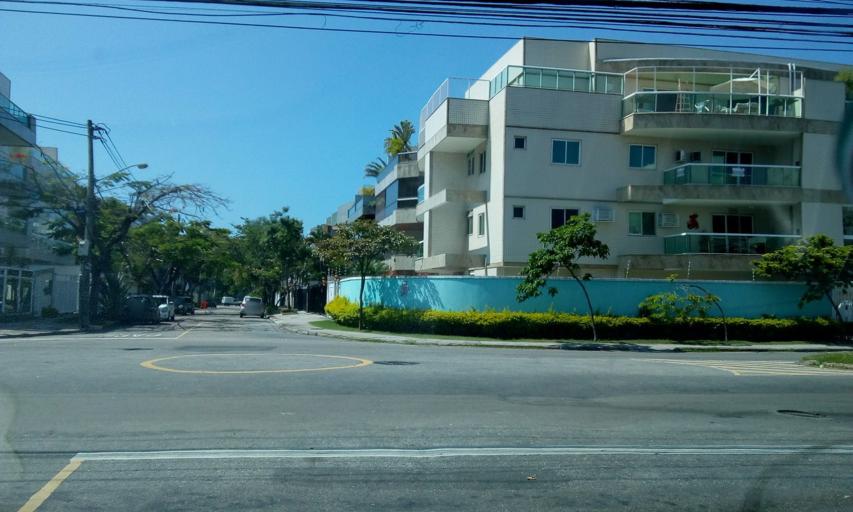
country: BR
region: Rio de Janeiro
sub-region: Nilopolis
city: Nilopolis
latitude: -23.0173
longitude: -43.4627
